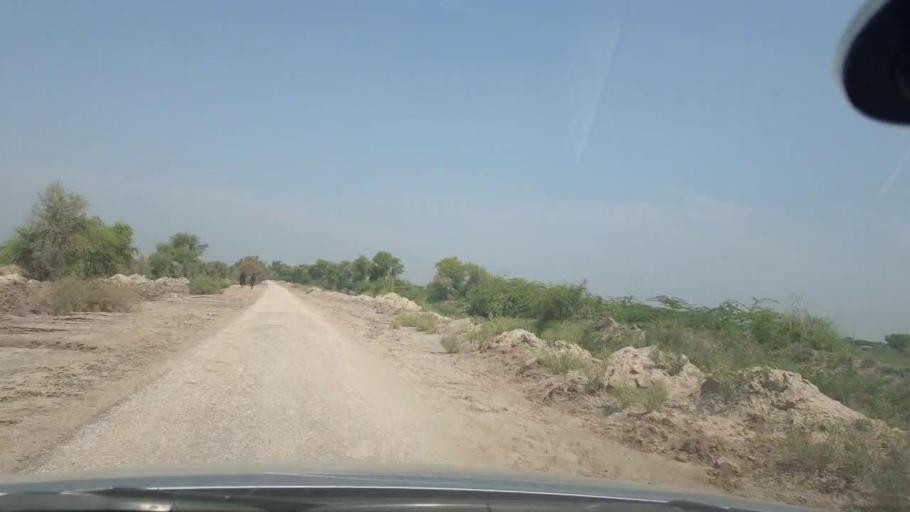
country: PK
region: Balochistan
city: Mehrabpur
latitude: 28.0864
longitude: 68.0406
